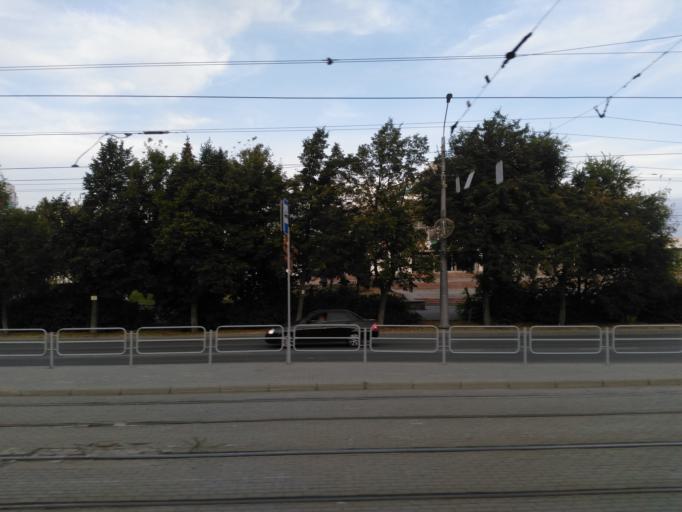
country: RU
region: Chelyabinsk
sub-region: Gorod Chelyabinsk
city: Chelyabinsk
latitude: 55.1727
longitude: 61.3997
